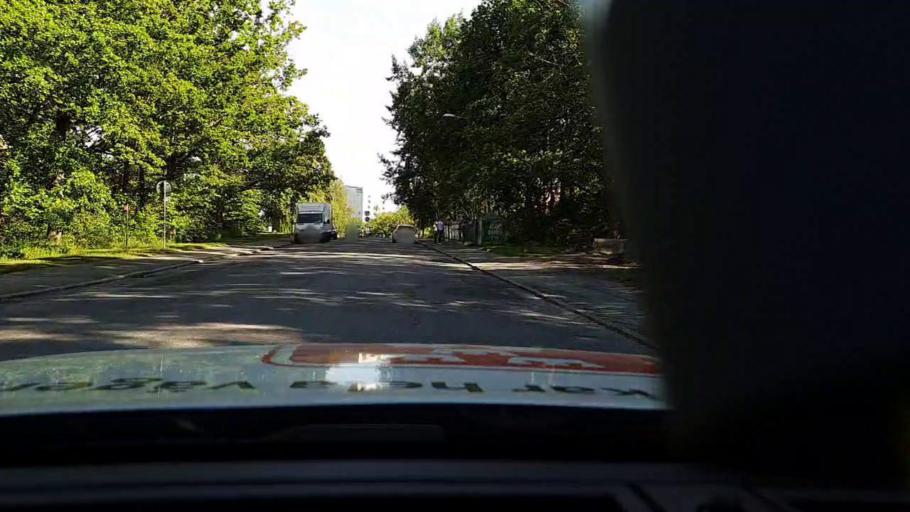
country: SE
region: Stockholm
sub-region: Stockholms Kommun
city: Arsta
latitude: 59.2673
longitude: 18.0312
